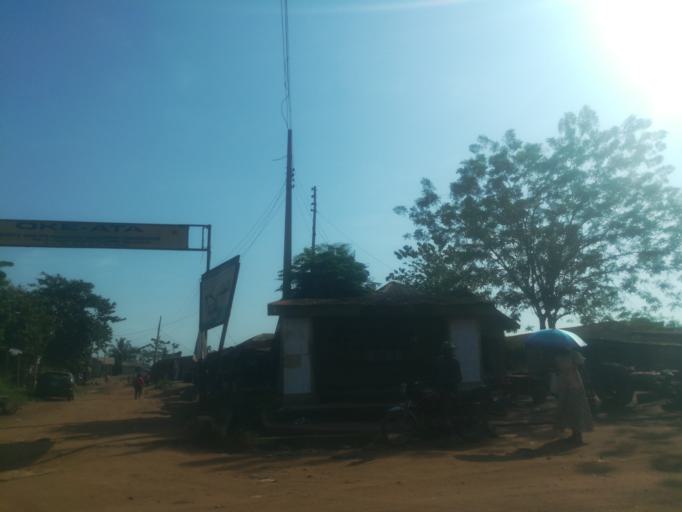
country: NG
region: Ogun
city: Abeokuta
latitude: 7.1405
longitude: 3.2689
